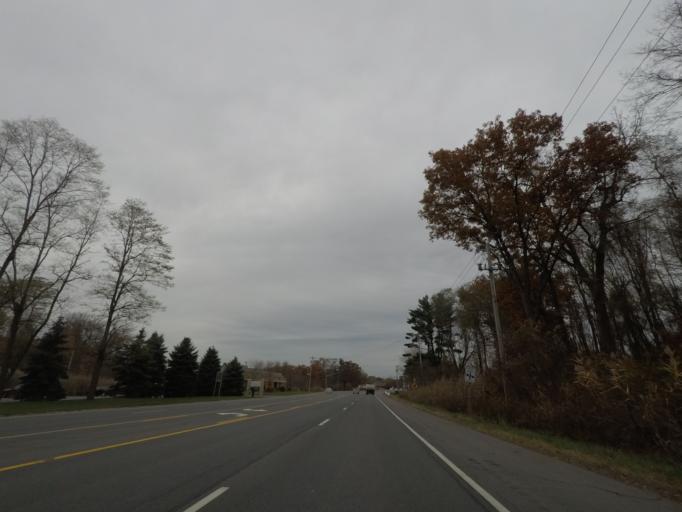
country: US
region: New York
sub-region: Saratoga County
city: Country Knolls
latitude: 42.8667
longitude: -73.7715
